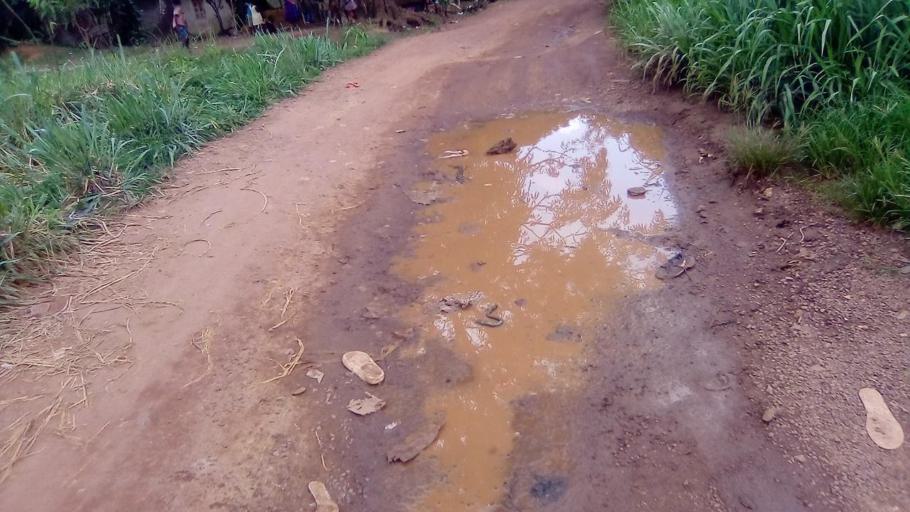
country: SL
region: Southern Province
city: Bo
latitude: 7.9579
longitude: -11.7260
